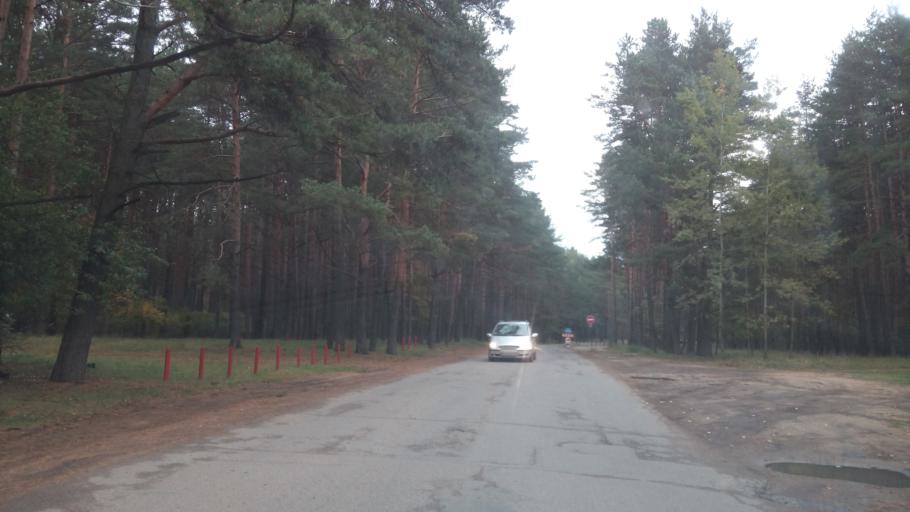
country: BY
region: Minsk
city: Zhdanovichy
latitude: 53.9513
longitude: 27.4352
